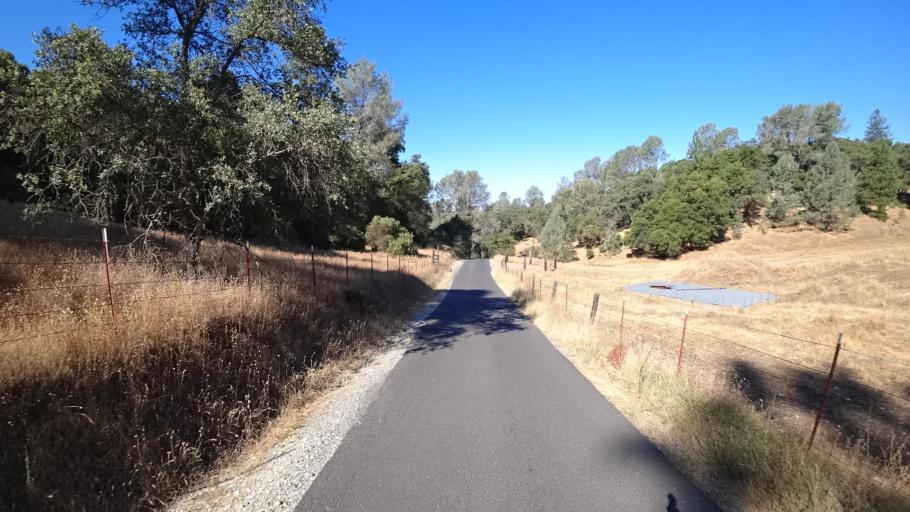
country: US
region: California
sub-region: Calaveras County
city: San Andreas
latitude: 38.2297
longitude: -120.6685
